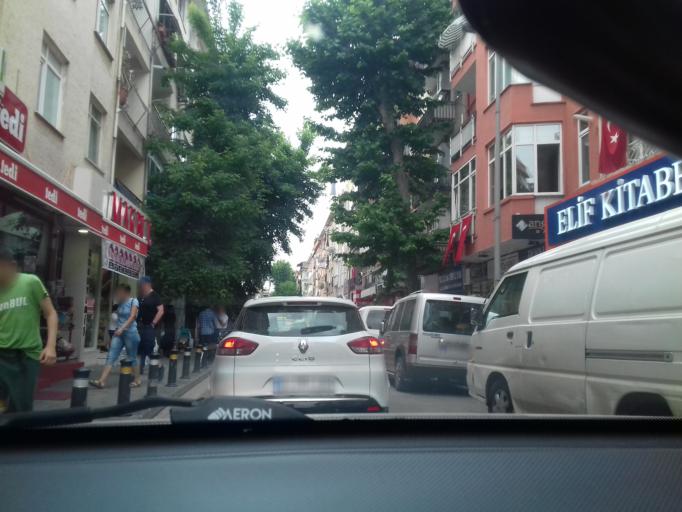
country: TR
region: Istanbul
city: Pendik
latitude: 40.8796
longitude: 29.2345
